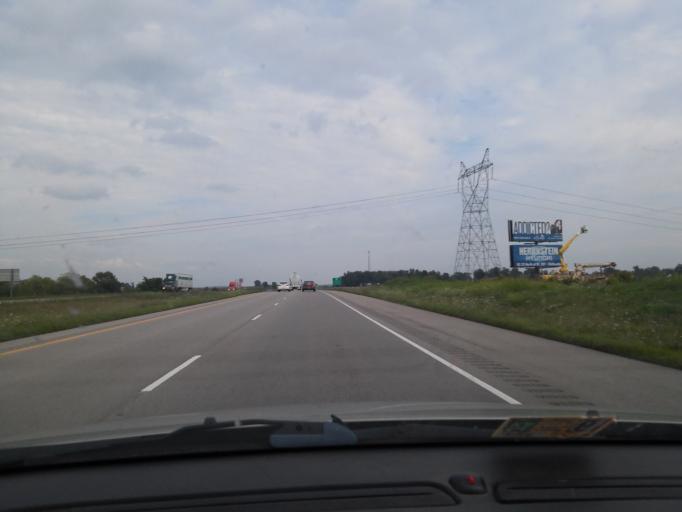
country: US
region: Ohio
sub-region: Ross County
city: Frankfort
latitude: 39.4553
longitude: -83.2292
